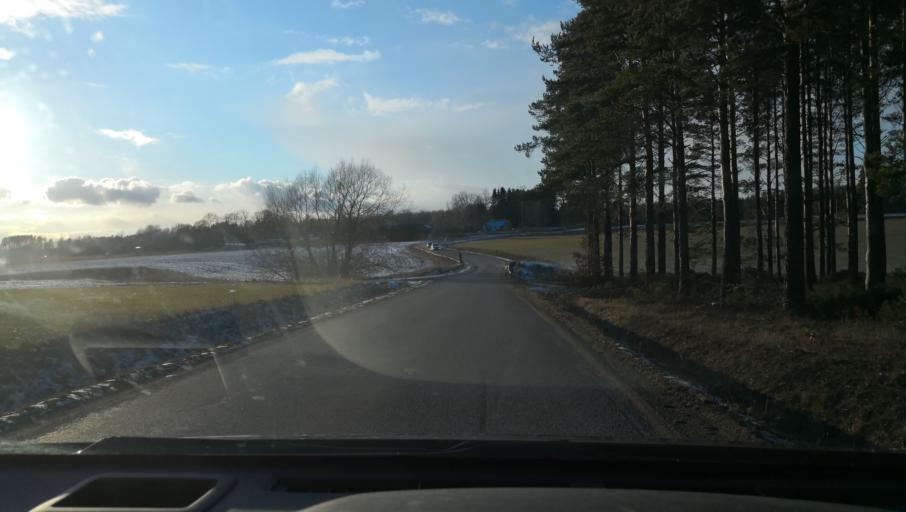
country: SE
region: Vaestmanland
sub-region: Vasteras
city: Tillberga
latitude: 59.6331
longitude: 16.6695
